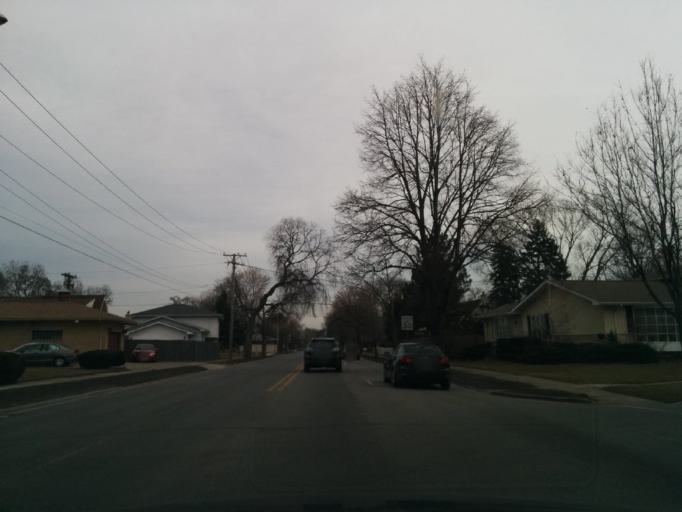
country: US
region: Illinois
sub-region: Cook County
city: Western Springs
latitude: 41.8192
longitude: -87.8848
